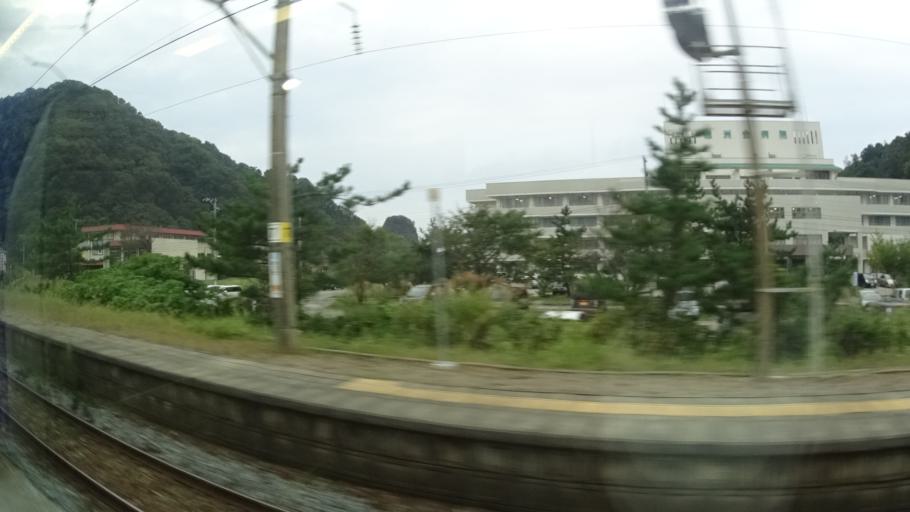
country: JP
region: Niigata
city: Murakami
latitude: 38.4902
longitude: 139.5176
